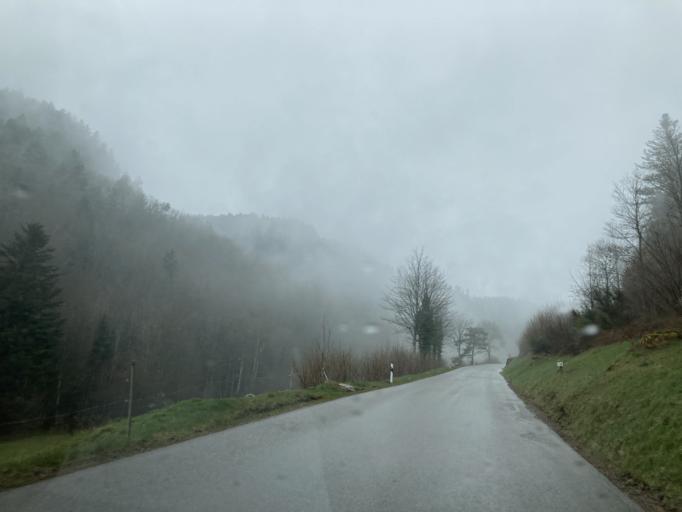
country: DE
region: Baden-Wuerttemberg
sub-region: Freiburg Region
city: Hornberg
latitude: 48.2288
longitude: 8.2680
